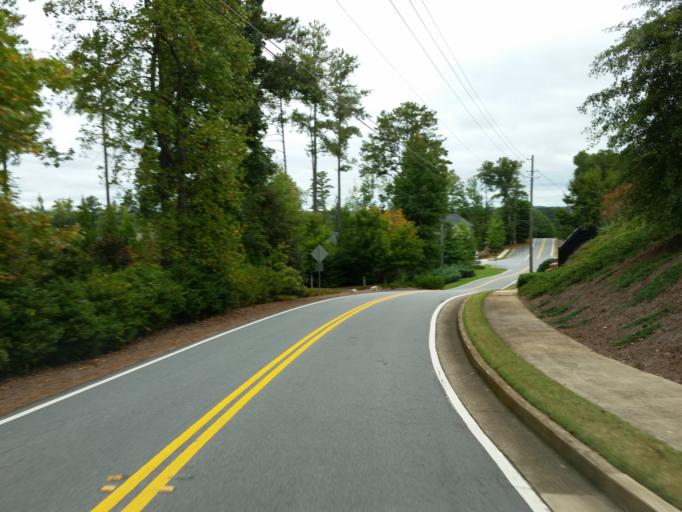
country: US
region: Georgia
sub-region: Cherokee County
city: Woodstock
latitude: 34.0836
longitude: -84.4714
